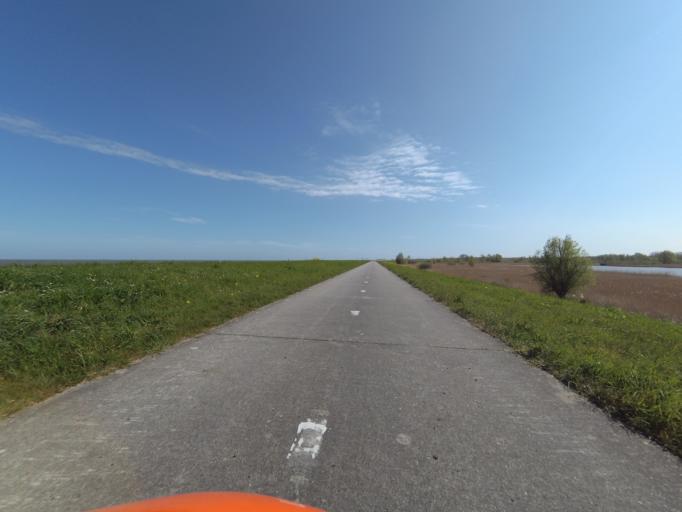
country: NL
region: Flevoland
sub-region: Gemeente Almere
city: Almere Stad
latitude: 52.4156
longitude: 5.2017
